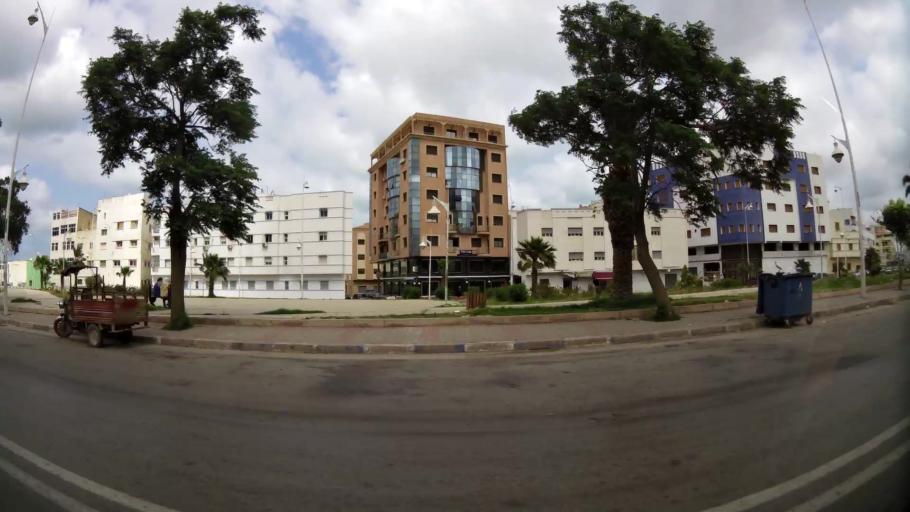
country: MA
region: Oriental
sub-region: Nador
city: Nador
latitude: 35.1815
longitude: -2.9285
